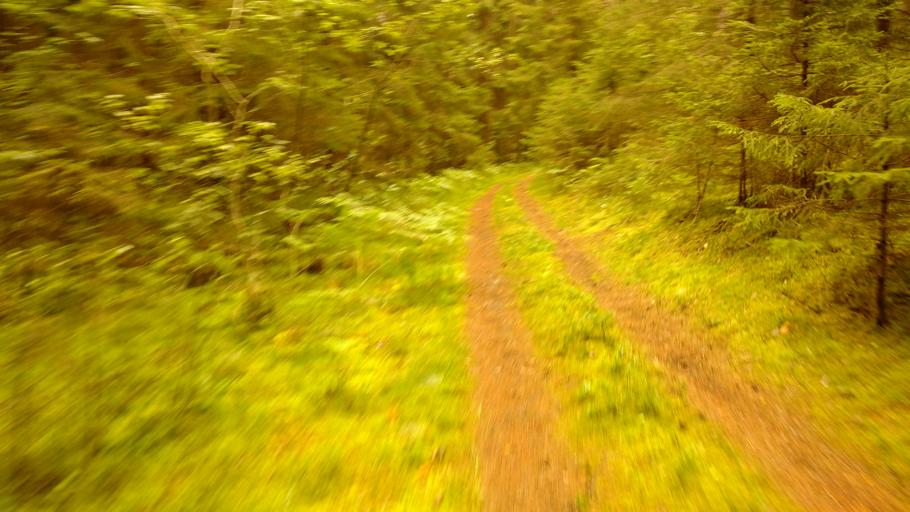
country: FI
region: Varsinais-Suomi
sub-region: Salo
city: Pertteli
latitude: 60.4033
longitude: 23.2178
